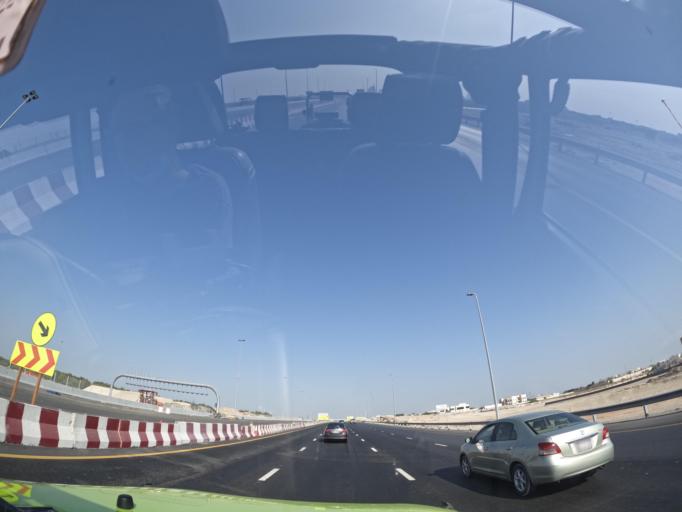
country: AE
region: Dubai
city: Dubai
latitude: 25.1433
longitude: 55.3459
